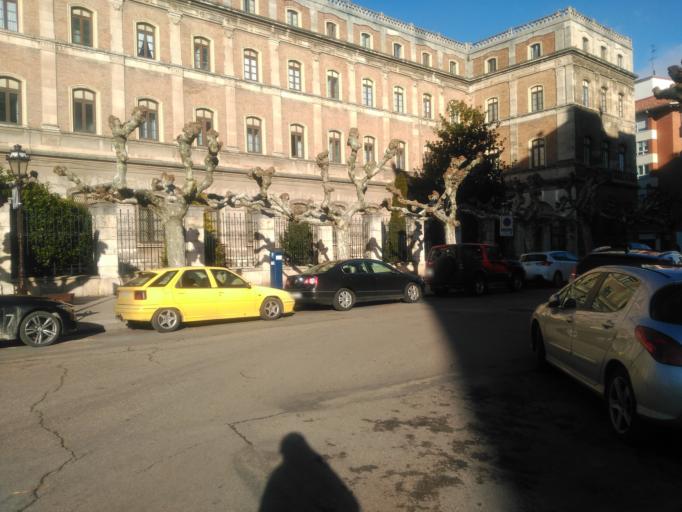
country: ES
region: Castille and Leon
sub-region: Provincia de Burgos
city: Burgos
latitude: 42.3392
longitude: -3.7063
